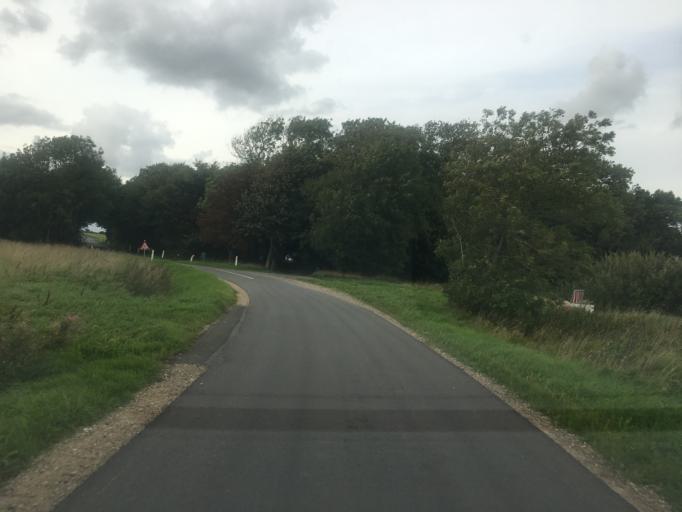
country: DE
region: Schleswig-Holstein
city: Aventoft
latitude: 54.9601
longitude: 8.8032
